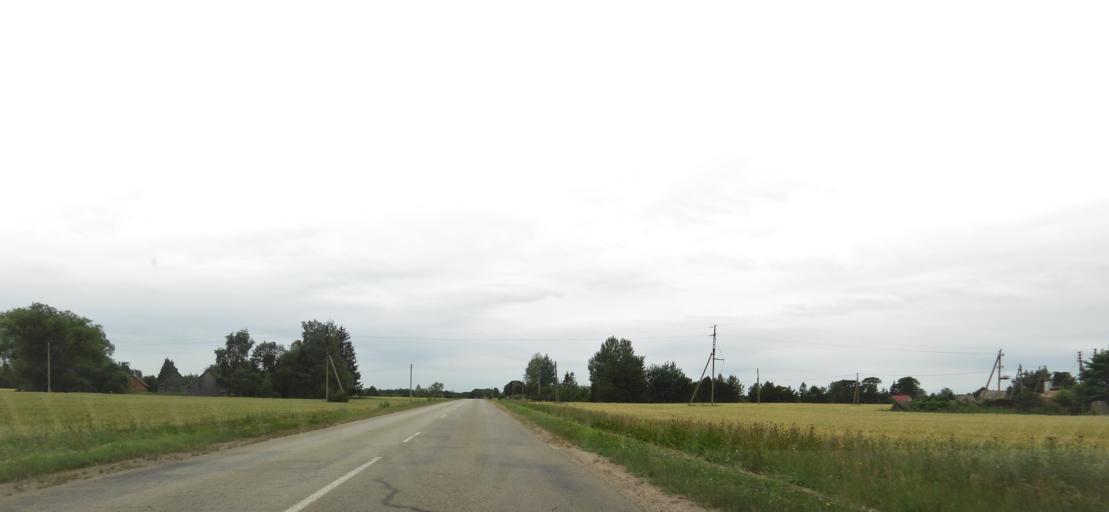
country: LT
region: Panevezys
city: Pasvalys
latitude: 56.0869
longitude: 24.4590
